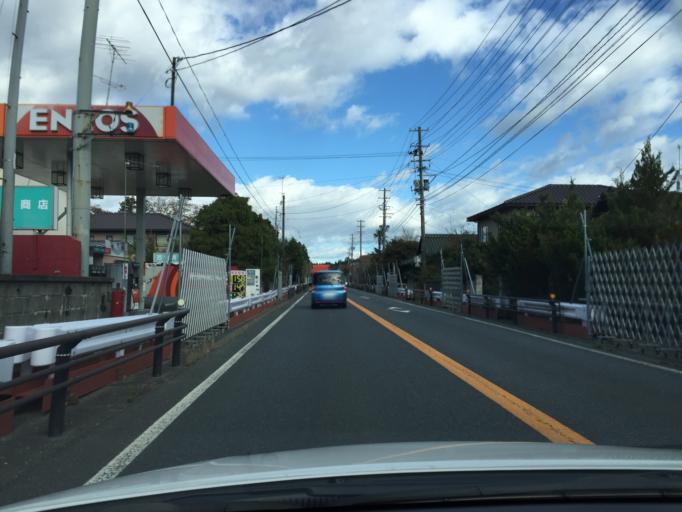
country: JP
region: Fukushima
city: Namie
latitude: 37.3827
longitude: 141.0086
